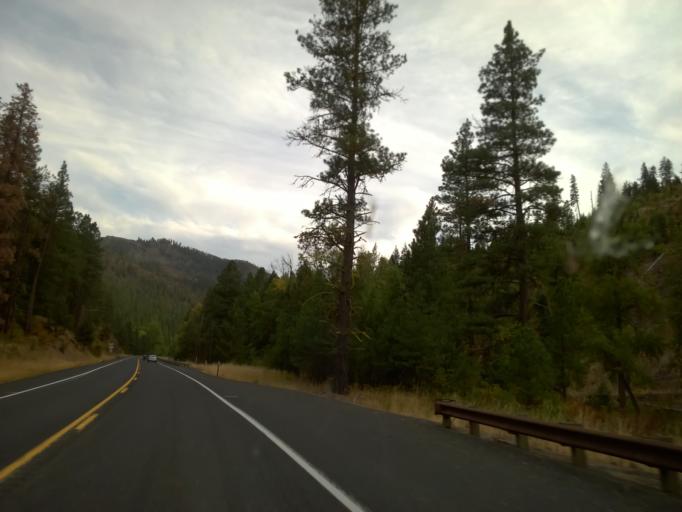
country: US
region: Washington
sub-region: Kittitas County
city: Cle Elum
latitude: 47.2411
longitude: -120.6969
